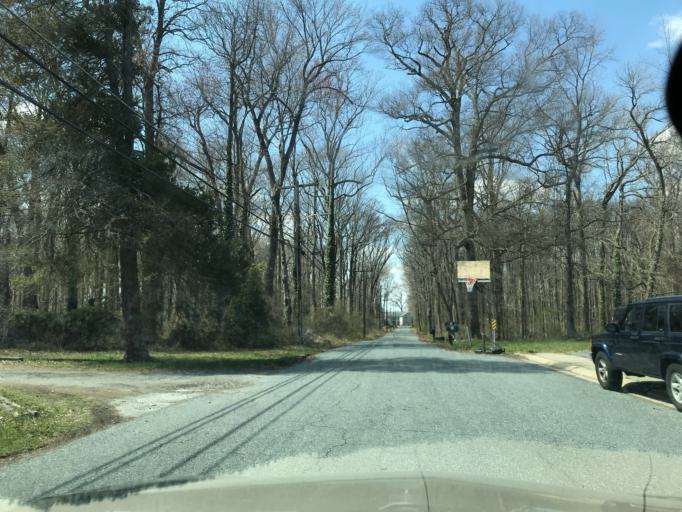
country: US
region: Maryland
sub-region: Harford County
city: Riverside
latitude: 39.4489
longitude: -76.2282
